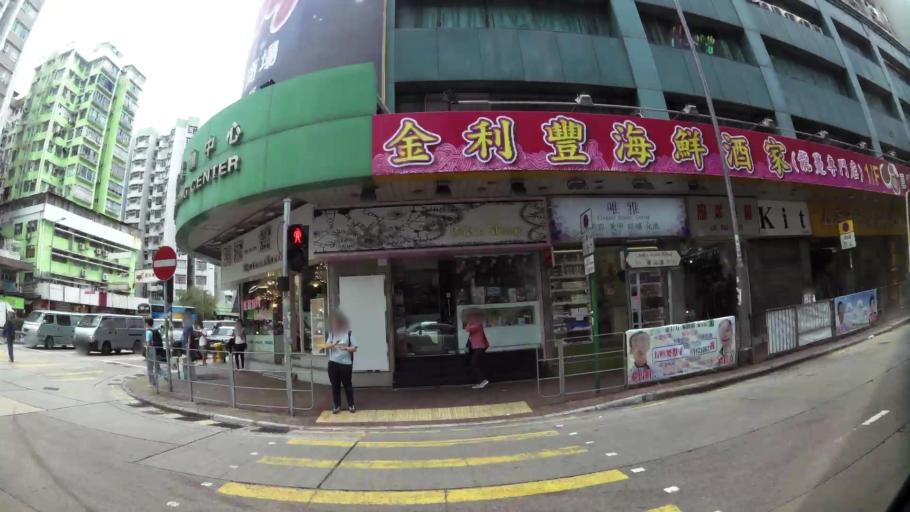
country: HK
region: Sham Shui Po
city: Sham Shui Po
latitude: 22.3363
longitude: 114.1591
